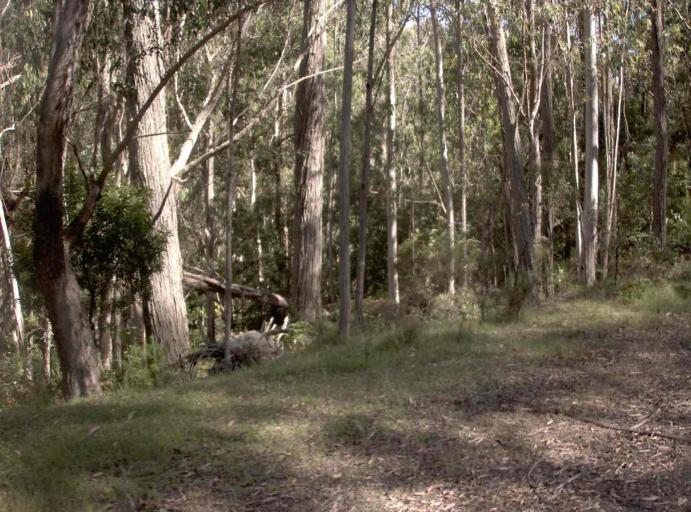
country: AU
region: New South Wales
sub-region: Bombala
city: Bombala
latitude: -37.2909
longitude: 148.7125
